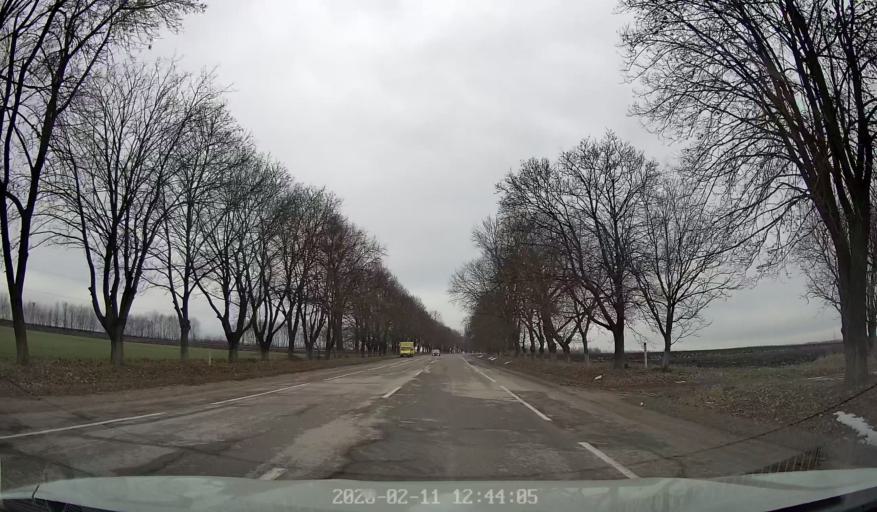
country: MD
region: Raionul Edinet
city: Edinet
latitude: 48.2409
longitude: 27.2039
